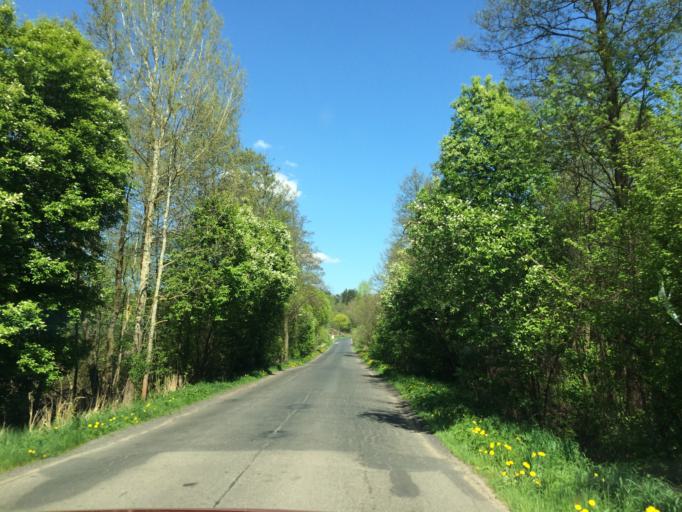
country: PL
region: Warmian-Masurian Voivodeship
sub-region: Powiat ilawski
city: Lubawa
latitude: 53.3960
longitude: 19.7389
